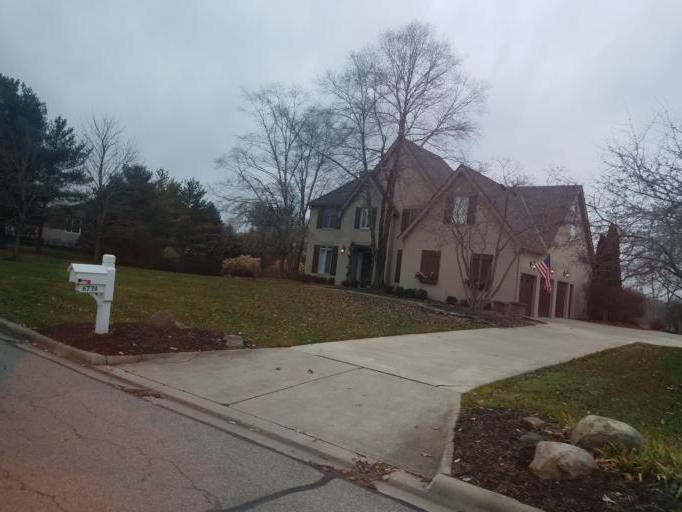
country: US
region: Ohio
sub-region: Franklin County
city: Westerville
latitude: 40.1672
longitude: -82.9484
